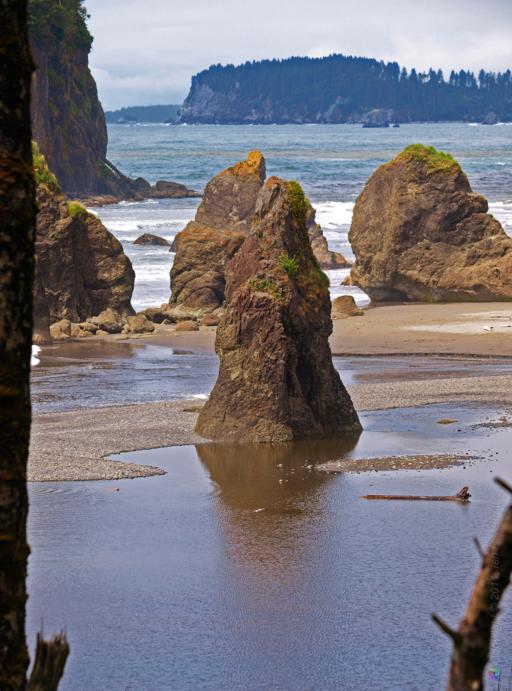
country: US
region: Washington
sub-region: Clallam County
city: Forks
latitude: 47.7105
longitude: -124.4145
